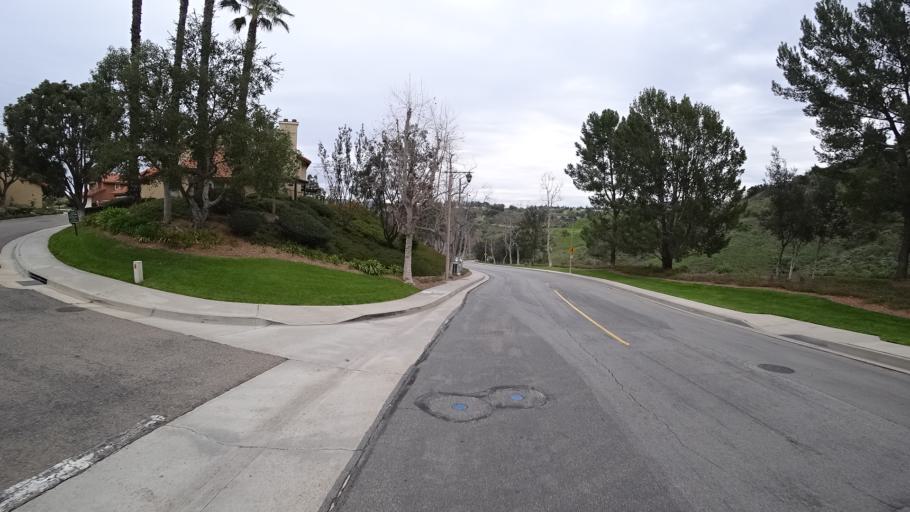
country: US
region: California
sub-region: Orange County
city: Villa Park
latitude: 33.8388
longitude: -117.7767
